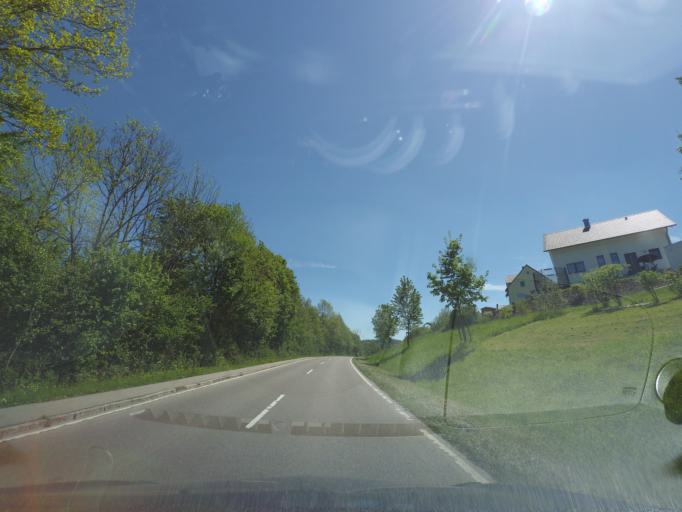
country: DE
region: Baden-Wuerttemberg
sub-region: Regierungsbezirk Stuttgart
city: Fichtenberg
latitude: 48.9936
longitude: 9.7080
